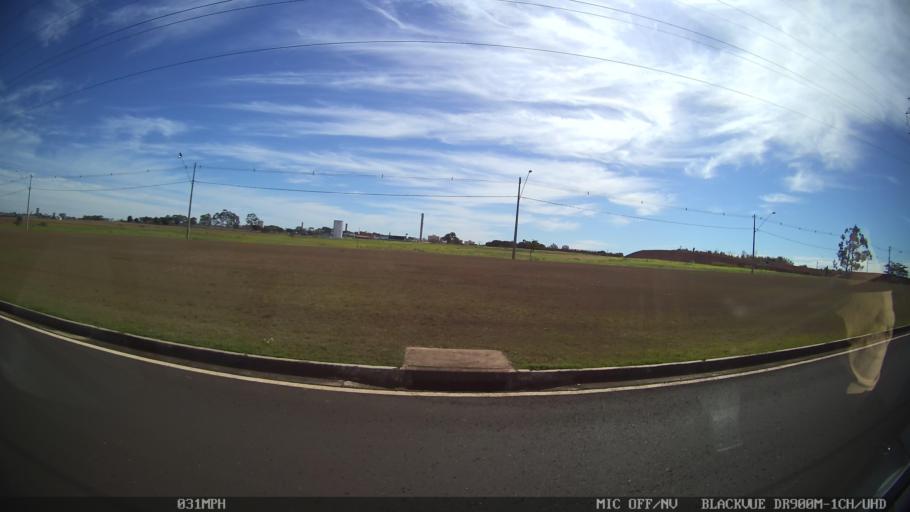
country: BR
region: Sao Paulo
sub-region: Sao Jose Do Rio Preto
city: Sao Jose do Rio Preto
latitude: -20.8520
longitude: -49.3758
